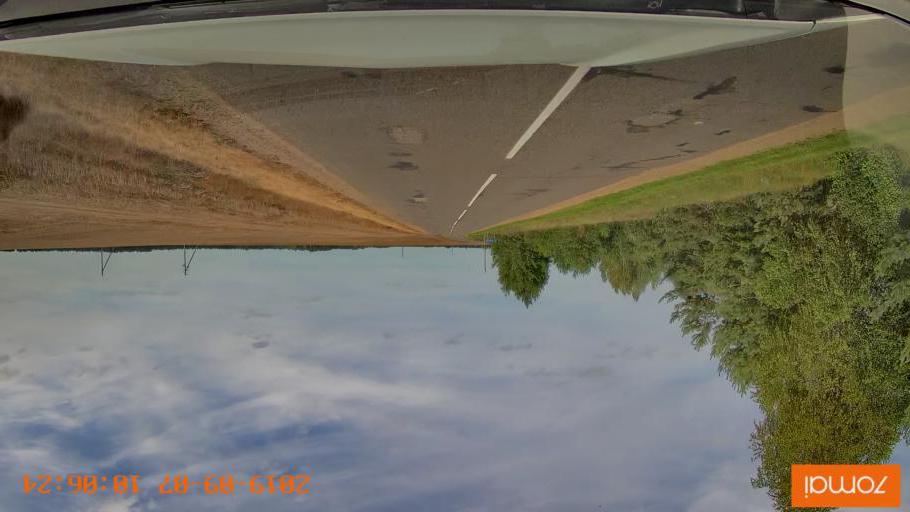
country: BY
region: Grodnenskaya
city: Voranava
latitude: 54.0612
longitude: 25.4032
